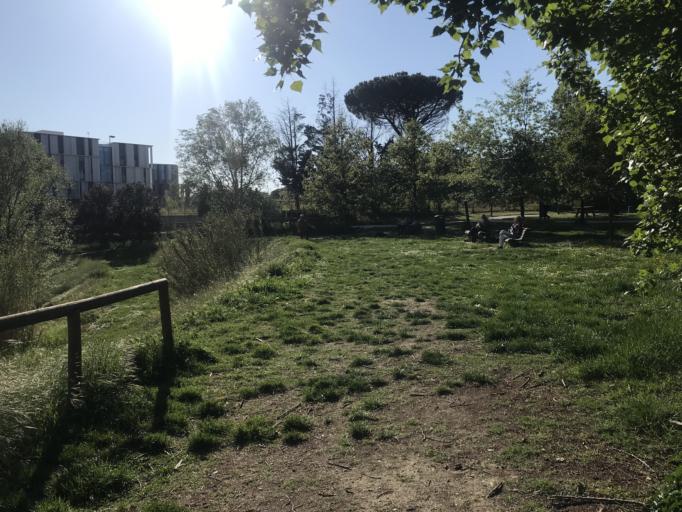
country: IT
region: Emilia-Romagna
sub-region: Provincia di Rimini
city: Rimini
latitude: 44.0495
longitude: 12.5699
